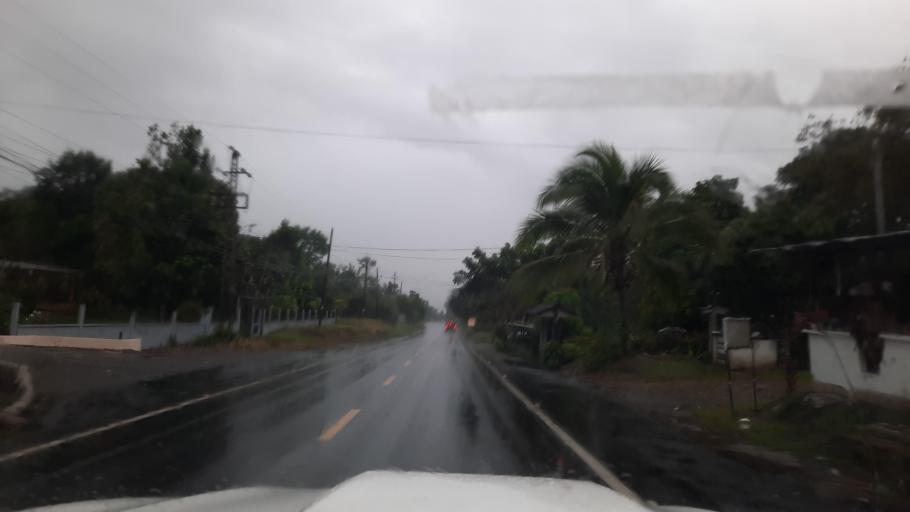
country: PA
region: Chiriqui
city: Sortova
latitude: 8.5732
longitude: -82.6345
